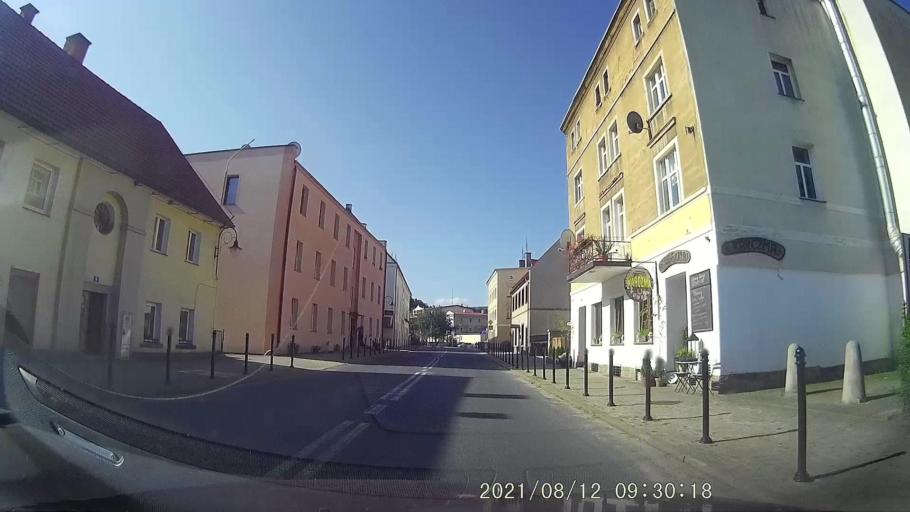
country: PL
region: Lower Silesian Voivodeship
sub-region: Powiat klodzki
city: Radkow
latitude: 50.4910
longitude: 16.4567
